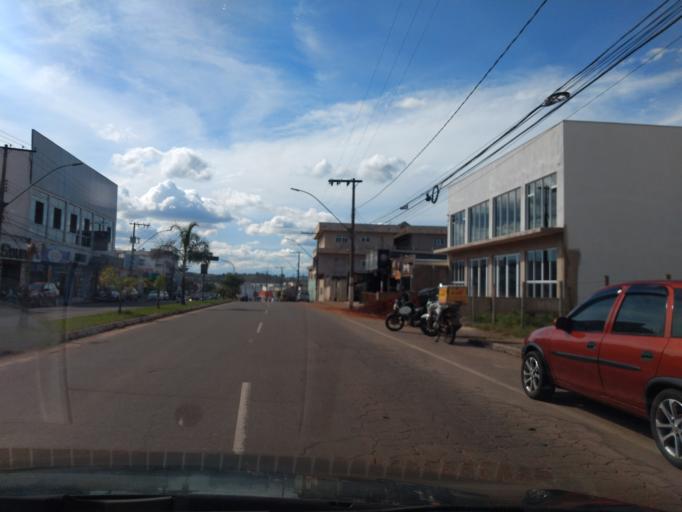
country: BR
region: Minas Gerais
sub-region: Tres Coracoes
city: Tres Coracoes
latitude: -21.6867
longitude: -45.2612
